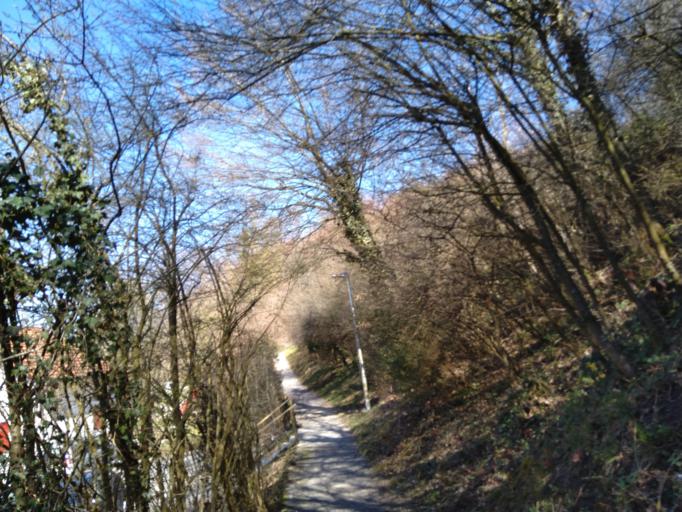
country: CH
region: Aargau
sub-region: Bezirk Kulm
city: Schoftland
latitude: 47.3098
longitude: 8.0553
